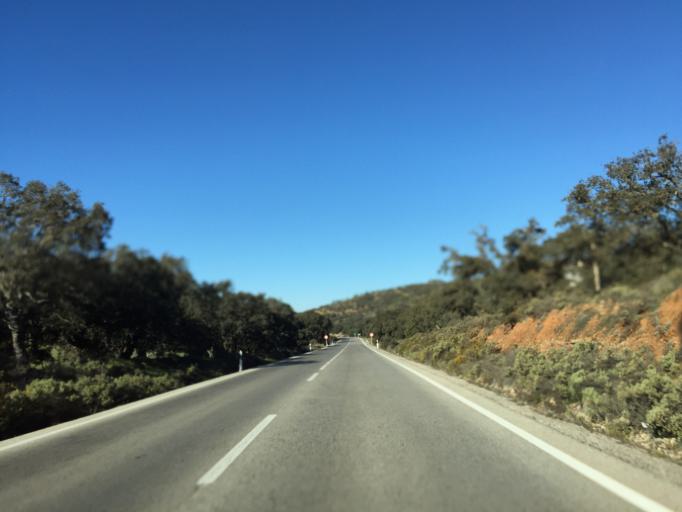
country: ES
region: Andalusia
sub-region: Provincia de Malaga
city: Cuevas del Becerro
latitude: 36.8315
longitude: -5.0811
